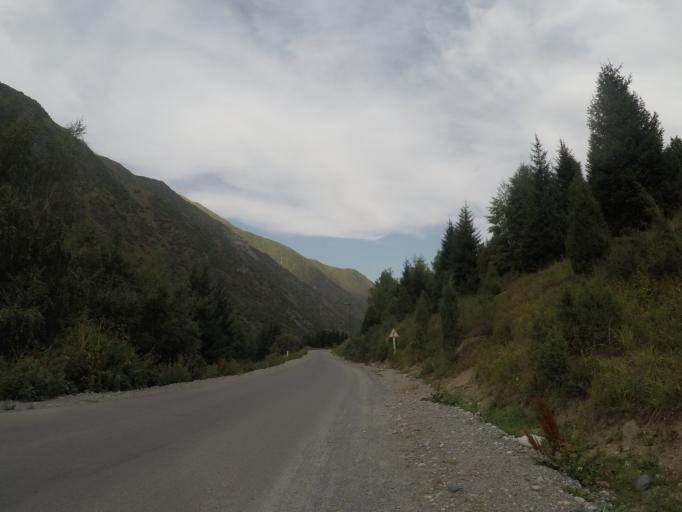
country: KG
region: Chuy
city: Bishkek
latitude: 42.5894
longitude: 74.4838
